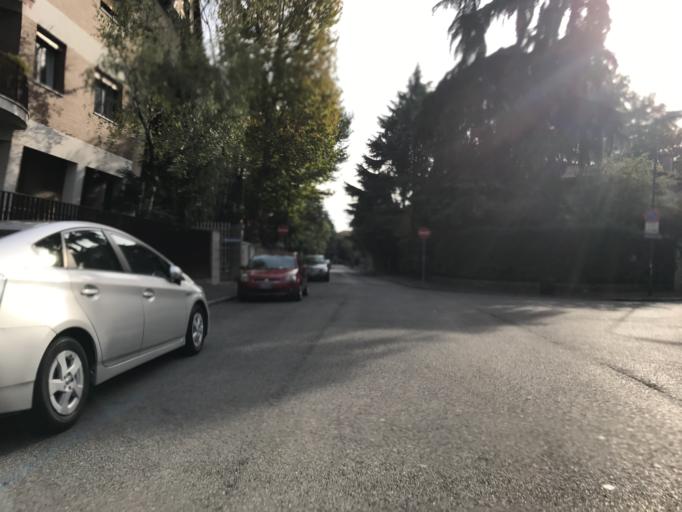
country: IT
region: Lombardy
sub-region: Citta metropolitana di Milano
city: Milano
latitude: 45.5005
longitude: 9.2018
